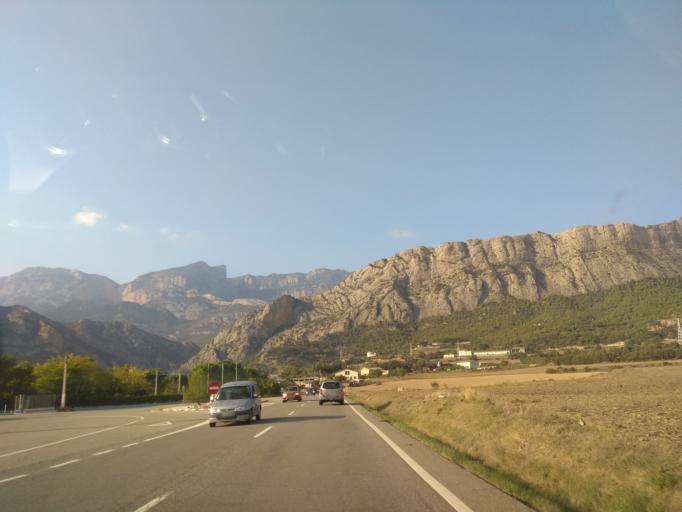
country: ES
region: Catalonia
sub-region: Provincia de Lleida
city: Oliana
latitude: 42.0767
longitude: 1.3063
